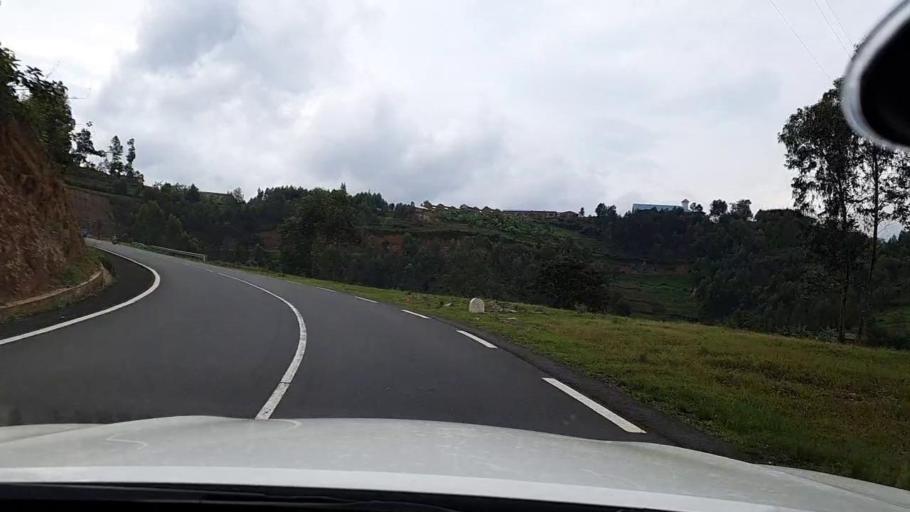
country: RW
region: Western Province
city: Kibuye
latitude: -2.1724
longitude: 29.2904
